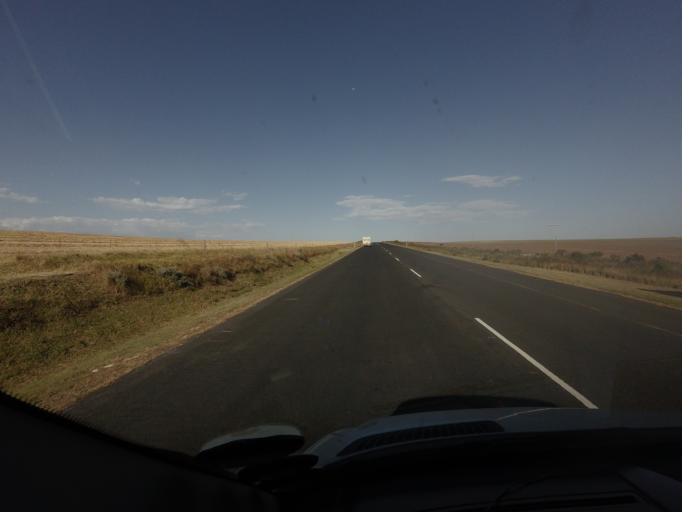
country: ZA
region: Western Cape
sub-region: Cape Winelands District Municipality
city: Ashton
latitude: -34.1410
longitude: 20.0137
